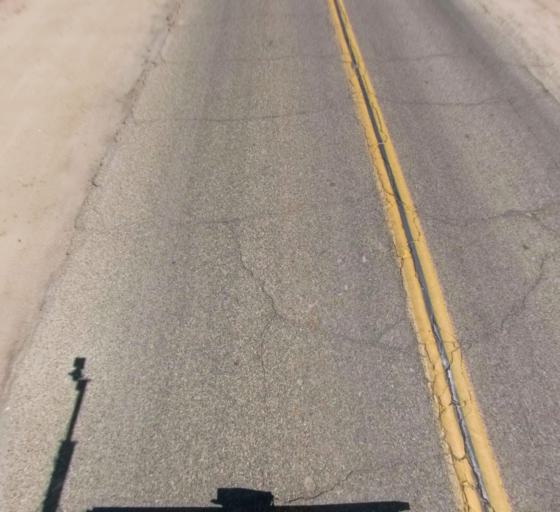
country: US
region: California
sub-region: Madera County
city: Parkwood
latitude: 36.9087
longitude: -120.0194
